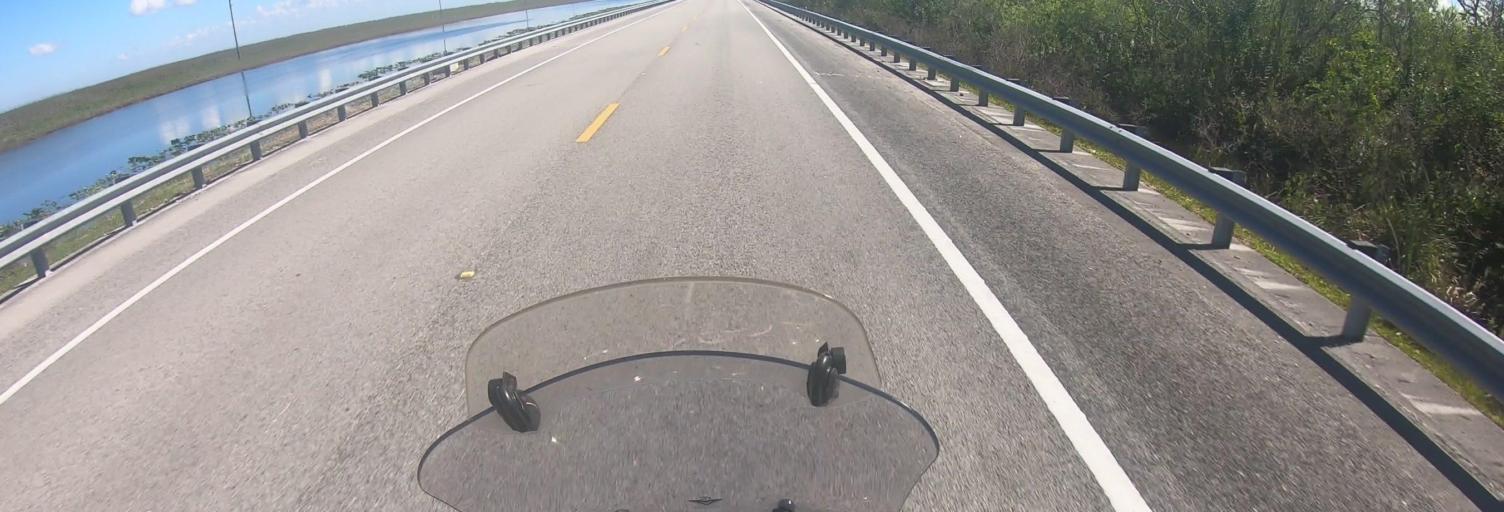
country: US
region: Florida
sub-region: Miami-Dade County
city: Kendall West
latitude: 25.7606
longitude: -80.5714
